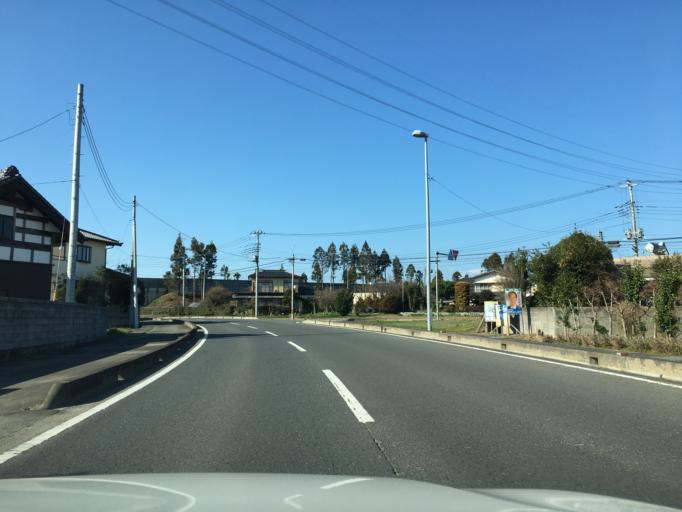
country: JP
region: Ibaraki
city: Mito-shi
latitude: 36.4220
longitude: 140.4351
